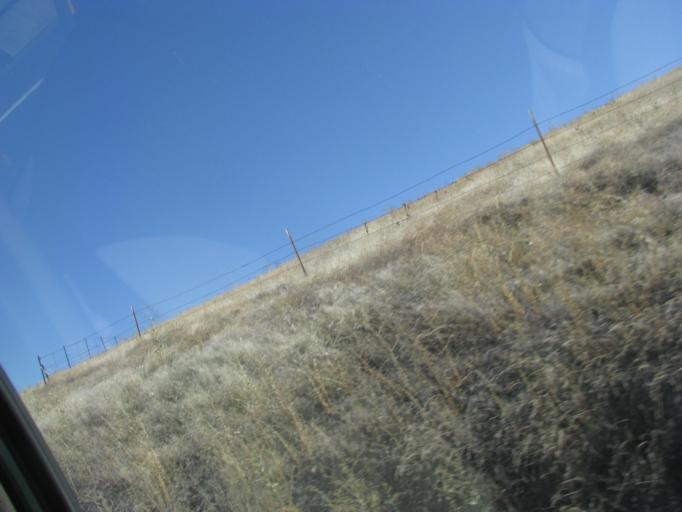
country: US
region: Washington
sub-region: Asotin County
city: Asotin
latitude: 46.3258
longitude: -117.0577
